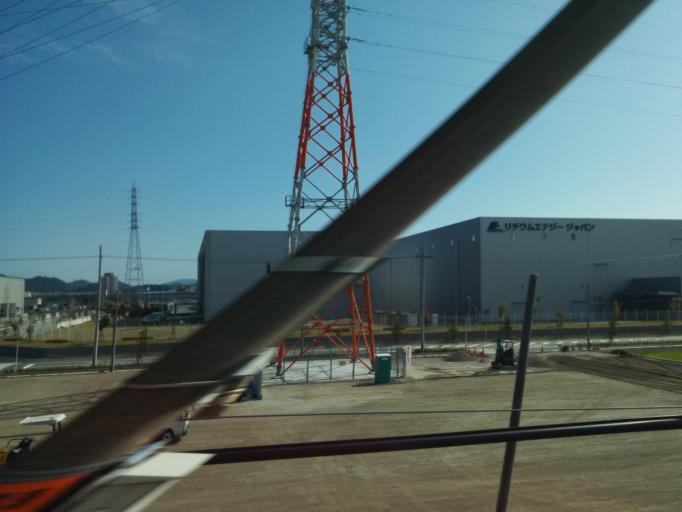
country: JP
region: Shiga Prefecture
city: Kusatsu
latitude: 35.0316
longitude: 135.9919
